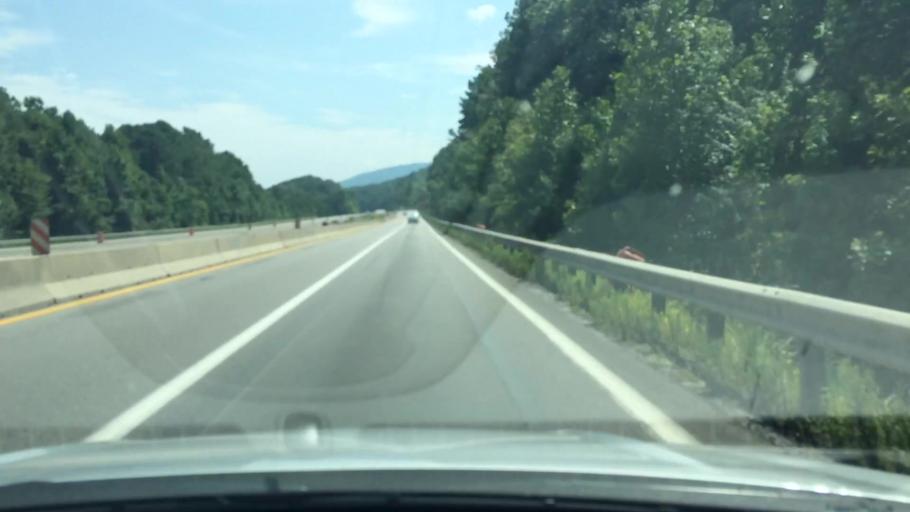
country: US
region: Tennessee
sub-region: Campbell County
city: Jacksboro
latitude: 36.3501
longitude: -84.2307
